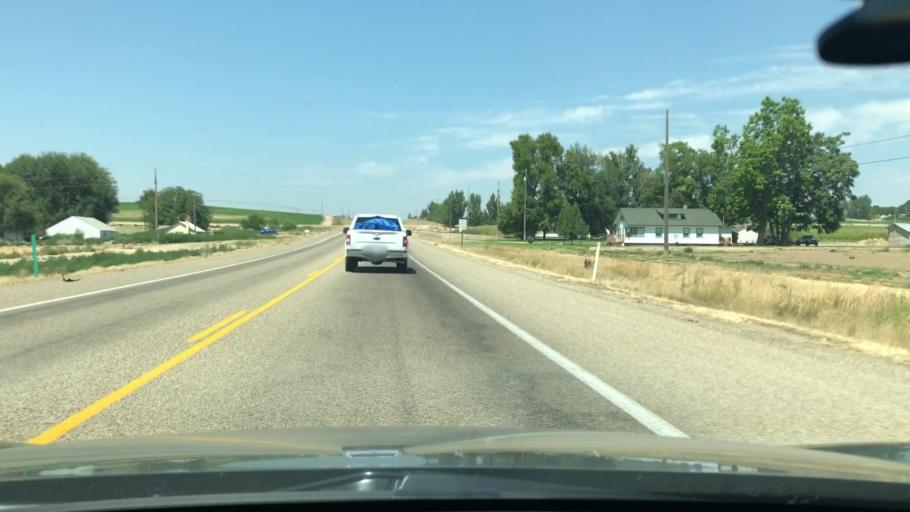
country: US
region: Idaho
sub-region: Canyon County
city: Parma
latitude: 43.8154
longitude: -116.9543
